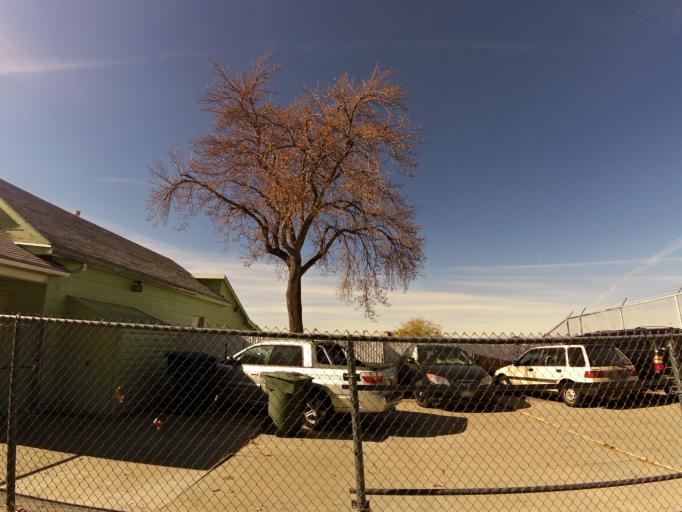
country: US
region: Utah
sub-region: Weber County
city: Ogden
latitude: 41.2301
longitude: -111.9687
